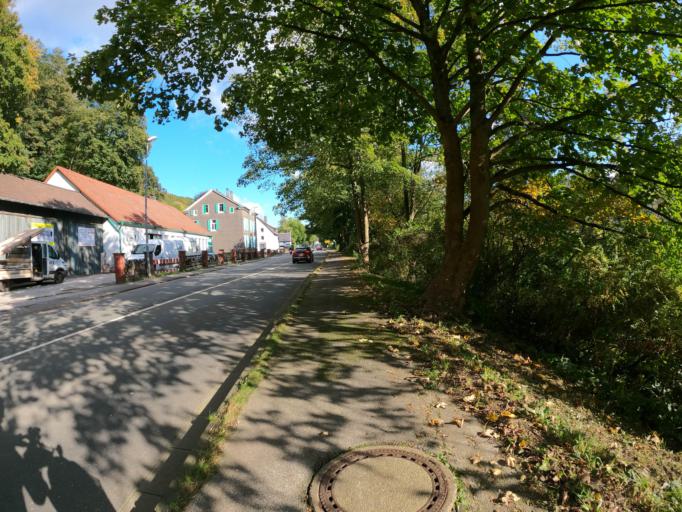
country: DE
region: North Rhine-Westphalia
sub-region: Regierungsbezirk Arnsberg
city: Schwelm
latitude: 51.2502
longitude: 7.2866
